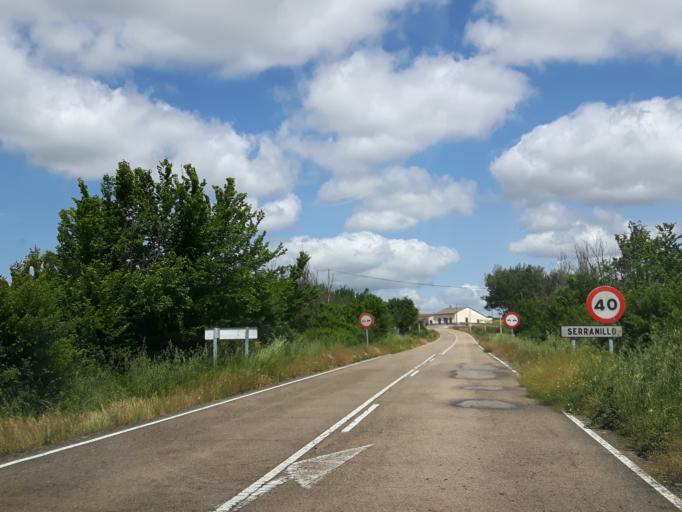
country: ES
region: Castille and Leon
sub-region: Provincia de Salamanca
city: Castillejo de Martin Viejo
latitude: 40.7017
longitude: -6.6700
